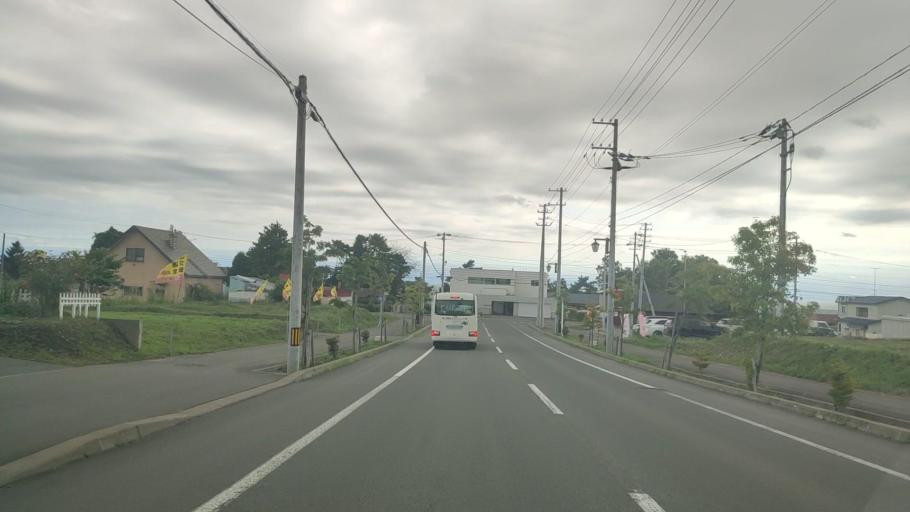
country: JP
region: Hokkaido
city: Date
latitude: 42.5513
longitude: 140.7699
